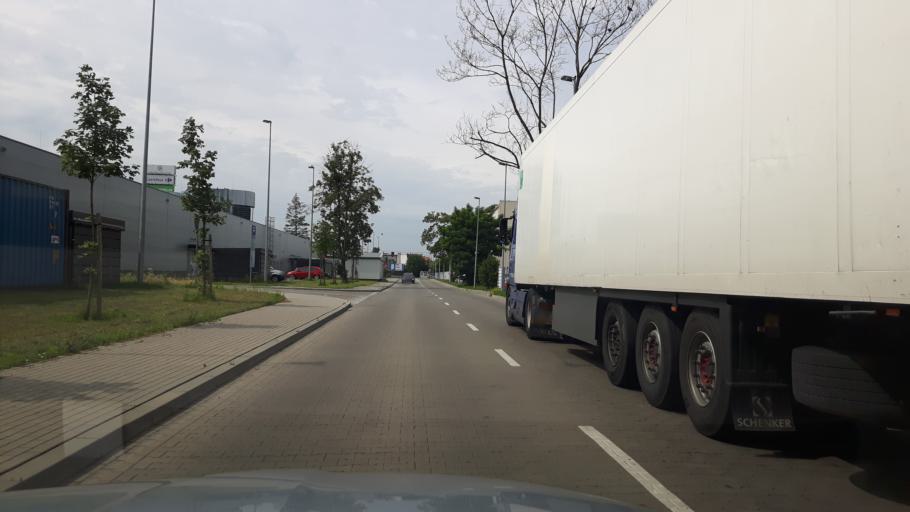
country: PL
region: Masovian Voivodeship
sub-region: Powiat wolominski
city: Nowe Lipiny
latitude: 52.3586
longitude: 21.2573
